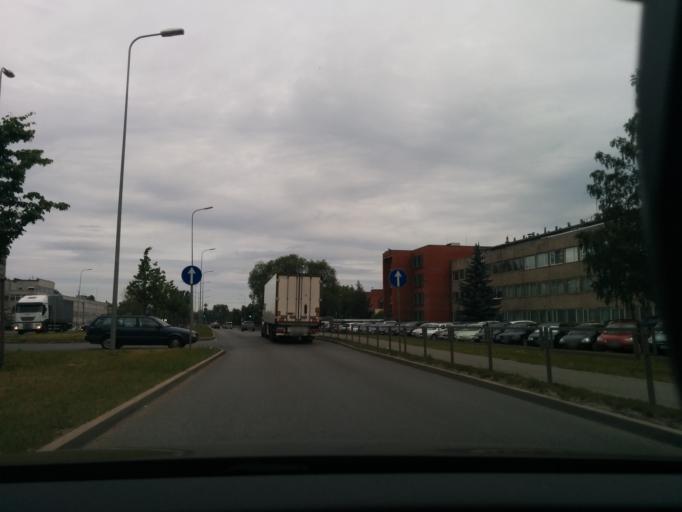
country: LV
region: Kekava
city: Balozi
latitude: 56.9194
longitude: 24.1951
